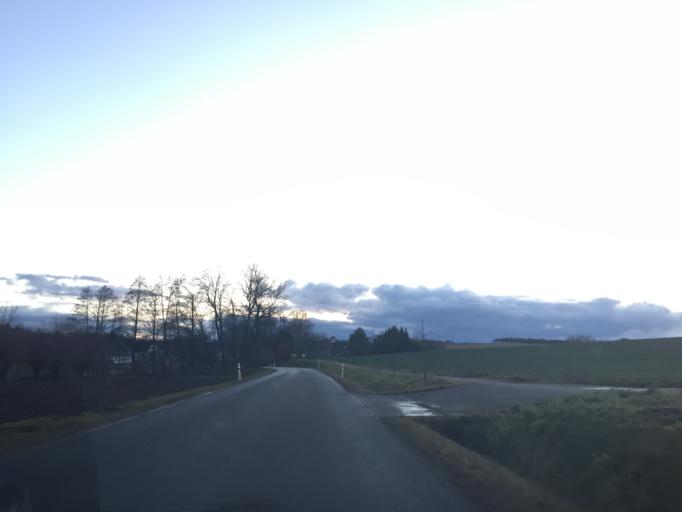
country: DE
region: Thuringia
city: Schmolln
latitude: 50.8819
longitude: 12.3336
